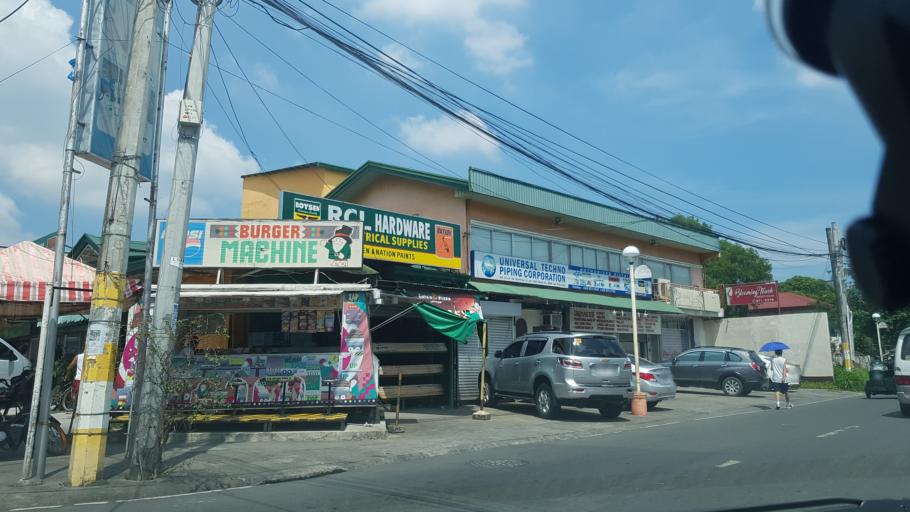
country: PH
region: Calabarzon
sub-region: Province of Rizal
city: Las Pinas
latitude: 14.4266
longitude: 120.9949
